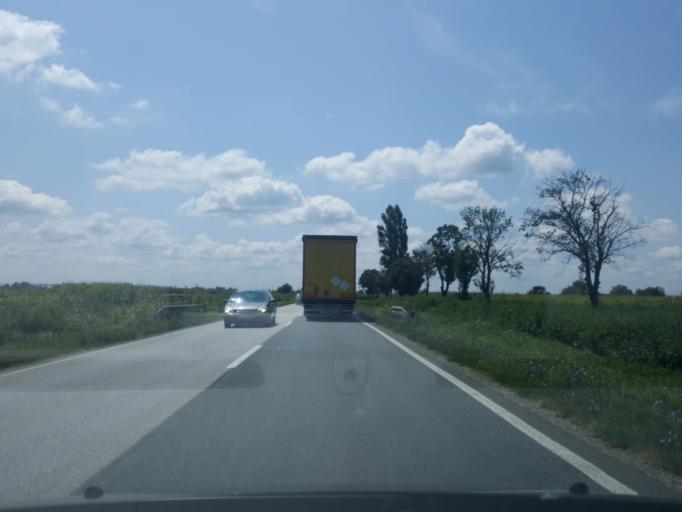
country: RS
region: Autonomna Pokrajina Vojvodina
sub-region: Sremski Okrug
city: Sremska Mitrovica
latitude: 44.9900
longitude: 19.6406
